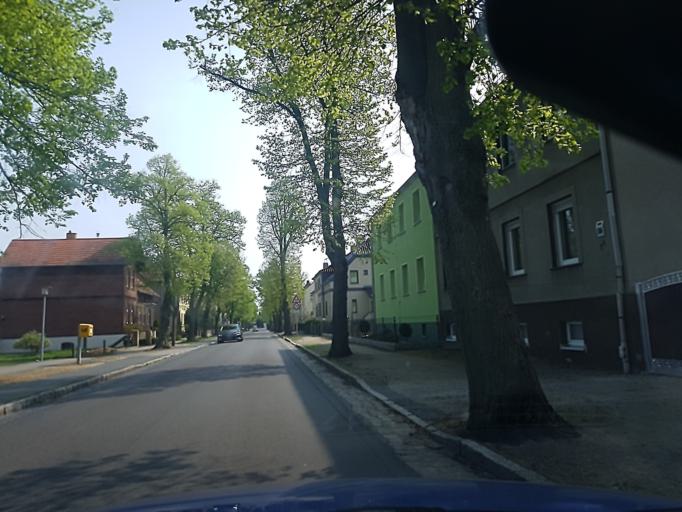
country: DE
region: Brandenburg
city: Falkenberg
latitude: 51.5870
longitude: 13.2307
